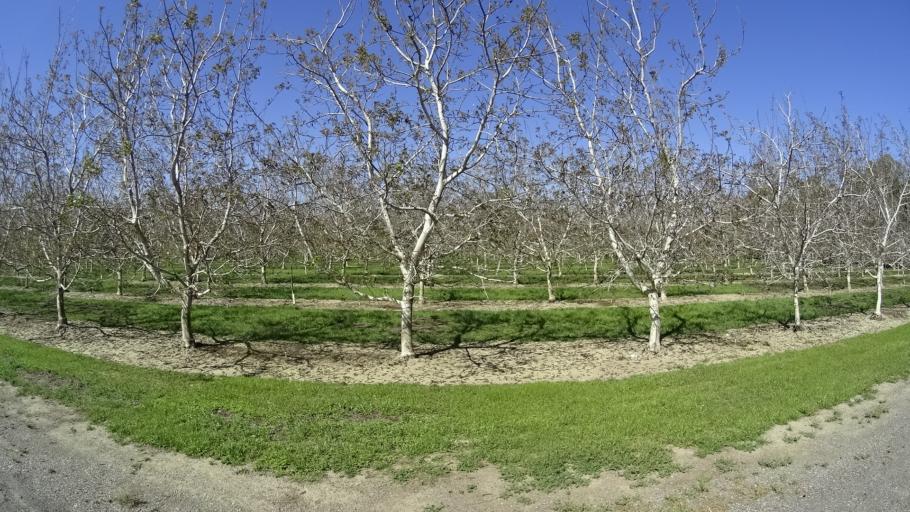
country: US
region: California
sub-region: Glenn County
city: Hamilton City
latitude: 39.7241
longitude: -122.0214
